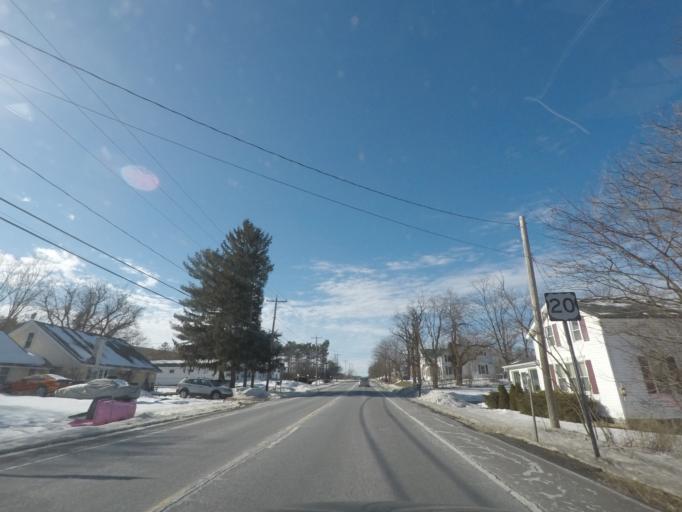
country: US
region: New York
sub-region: Albany County
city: Altamont
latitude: 42.7402
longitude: -74.0166
